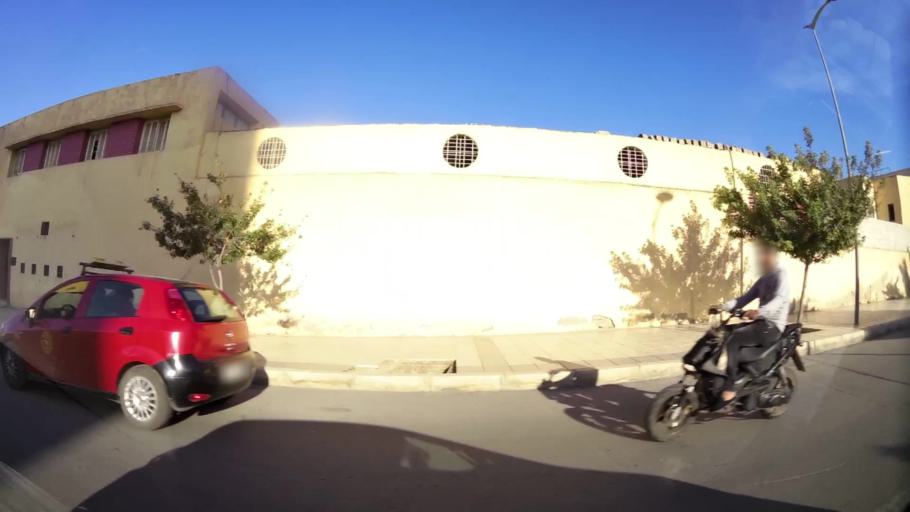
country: MA
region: Oriental
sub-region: Oujda-Angad
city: Oujda
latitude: 34.6954
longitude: -1.9109
